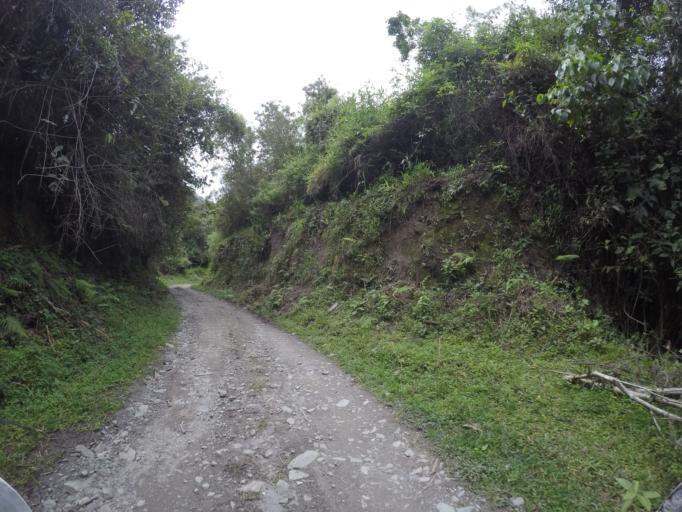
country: CO
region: Tolima
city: Cajamarca
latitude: 4.5323
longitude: -75.4113
